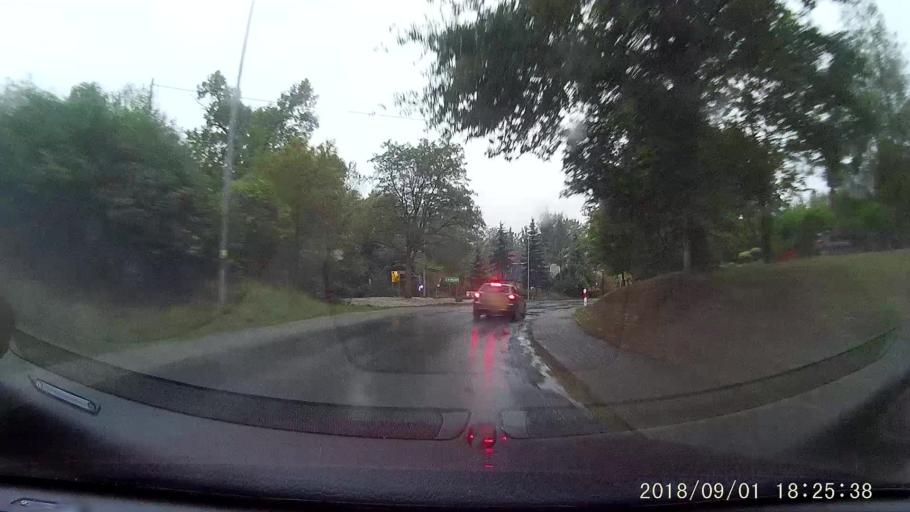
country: PL
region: Lower Silesian Voivodeship
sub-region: Powiat zgorzelecki
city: Piensk
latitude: 51.2289
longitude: 15.0312
